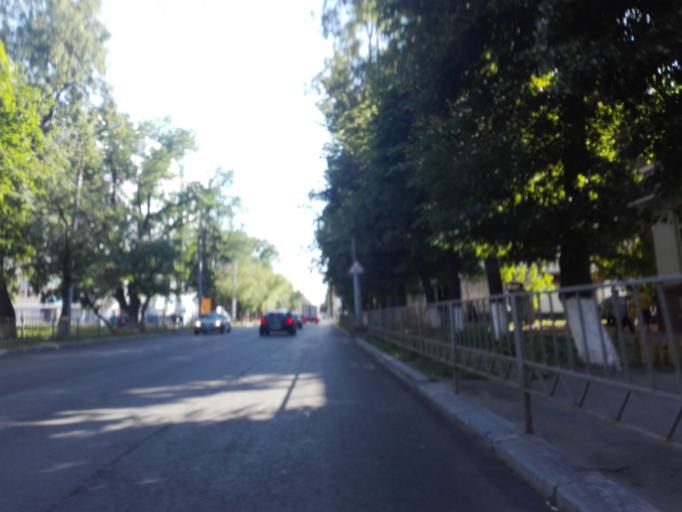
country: RU
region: Orjol
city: Orel
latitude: 52.9730
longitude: 36.0596
